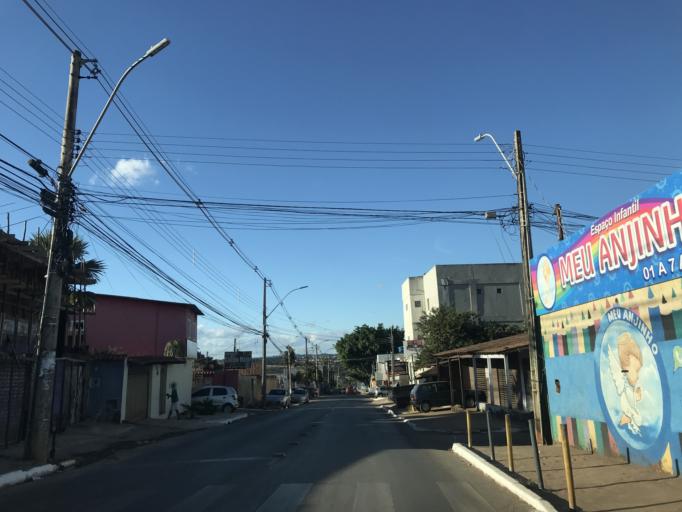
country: BR
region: Federal District
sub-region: Brasilia
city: Brasilia
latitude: -15.8956
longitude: -47.7858
